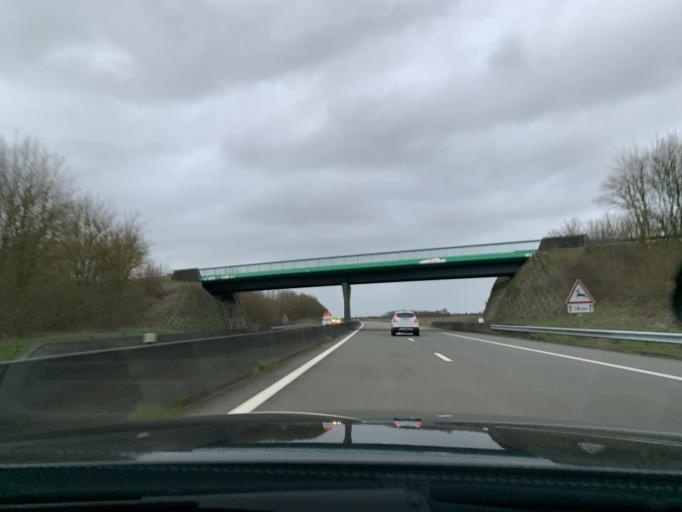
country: FR
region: Picardie
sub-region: Departement de la Somme
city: Conty
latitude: 49.7091
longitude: 2.2390
